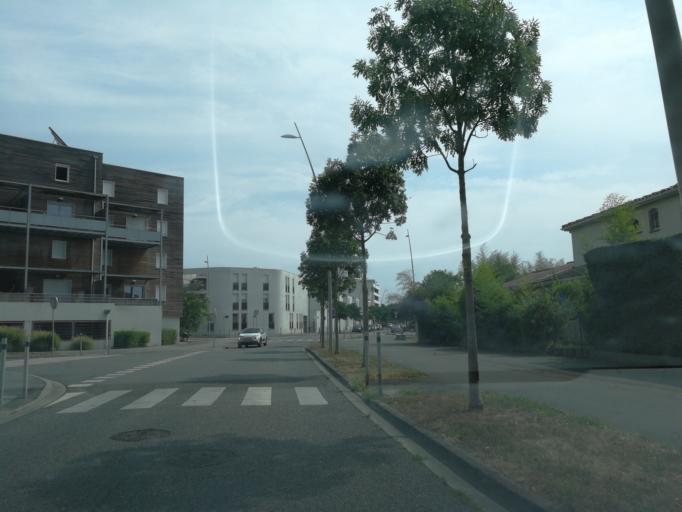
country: FR
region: Midi-Pyrenees
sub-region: Departement de la Haute-Garonne
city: Beauzelle
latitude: 43.6520
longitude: 1.3714
